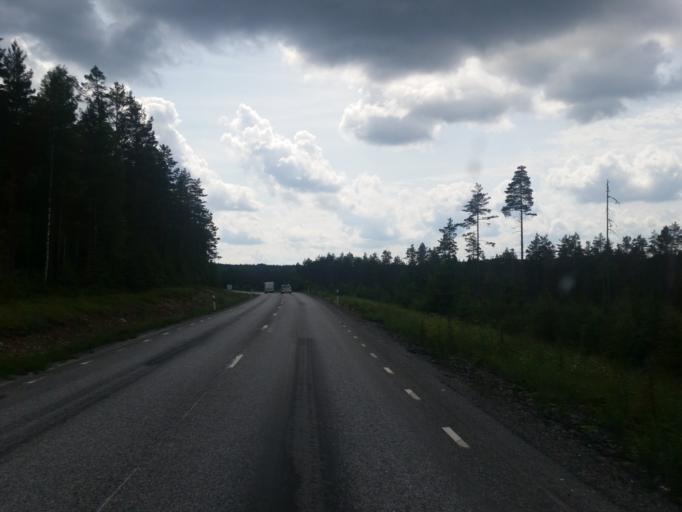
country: SE
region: OErebro
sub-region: Ljusnarsbergs Kommun
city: Kopparberg
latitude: 59.9494
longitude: 15.0209
